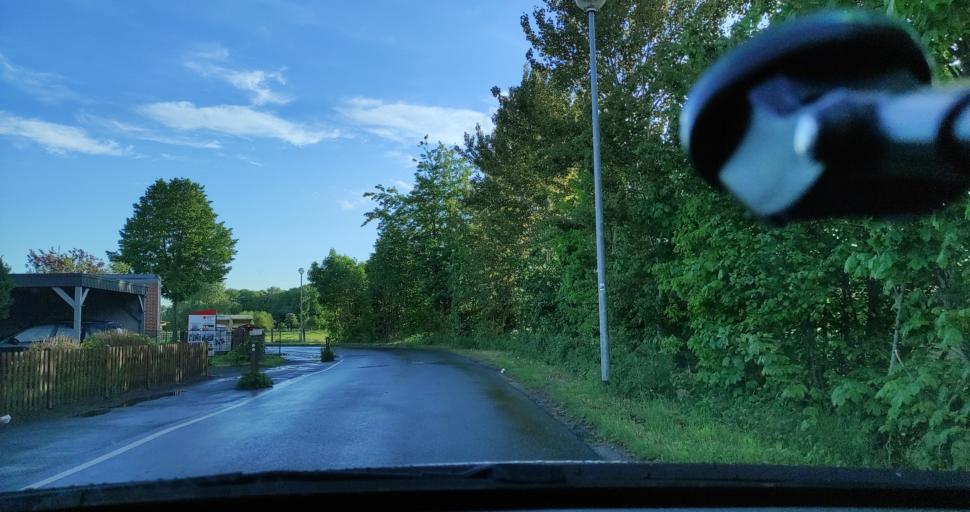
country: DE
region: North Rhine-Westphalia
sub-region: Regierungsbezirk Munster
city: Greven
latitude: 52.1055
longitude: 7.5830
